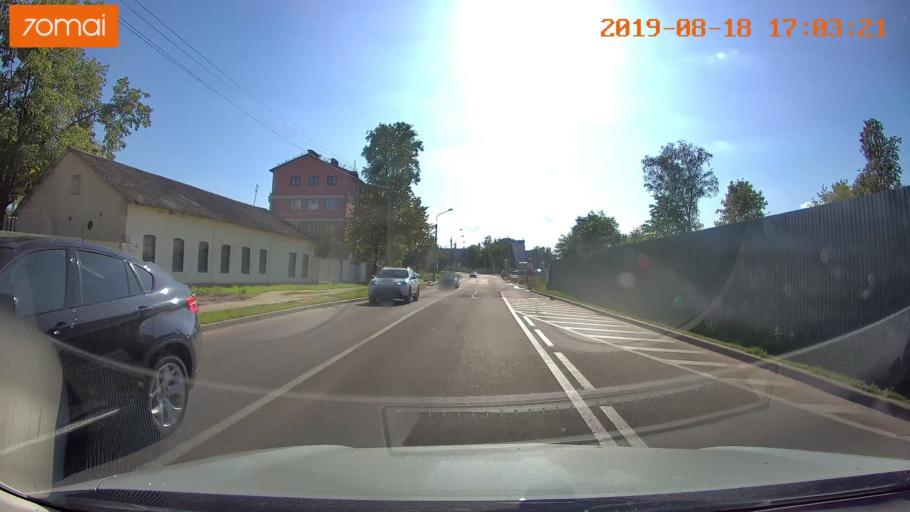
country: BY
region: Minsk
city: Minsk
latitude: 53.9036
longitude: 27.5230
